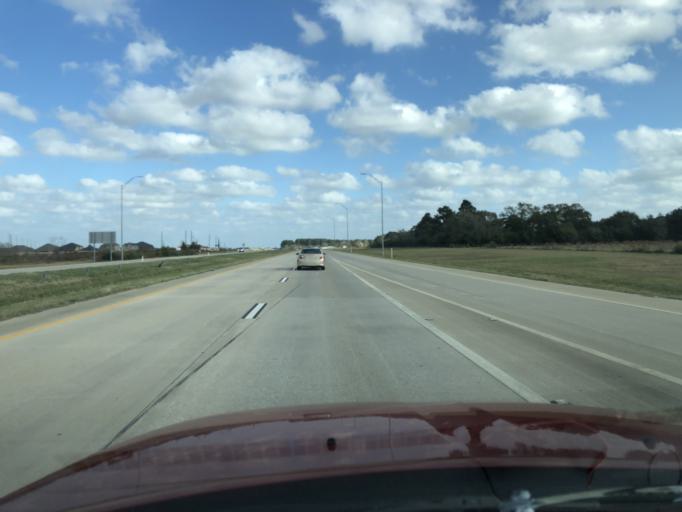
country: US
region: Texas
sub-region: Harris County
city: Cypress
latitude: 30.0532
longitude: -95.7298
